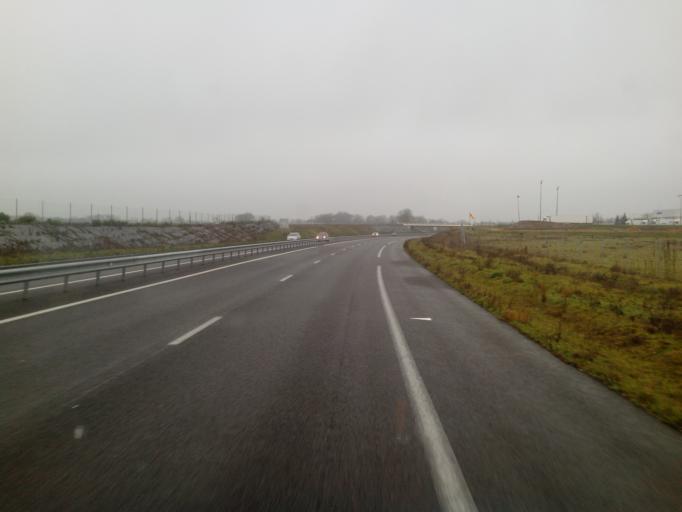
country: FR
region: Poitou-Charentes
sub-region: Departement de la Vienne
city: Savigny-Levescault
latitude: 46.4874
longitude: 0.5073
